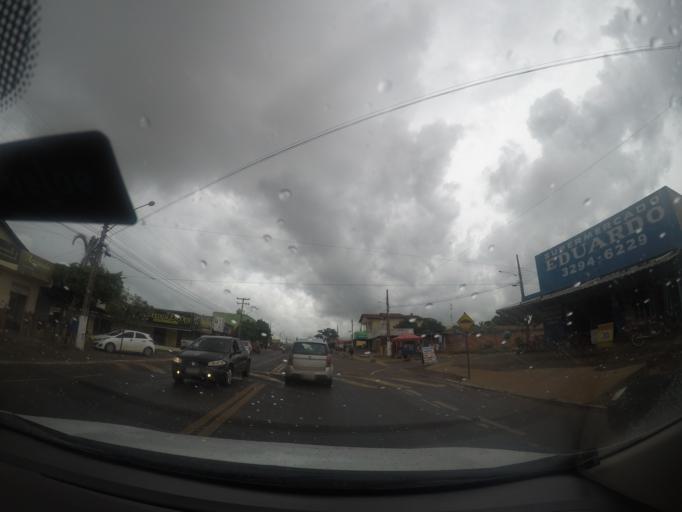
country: BR
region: Goias
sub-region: Trindade
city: Trindade
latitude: -16.6383
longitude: -49.3903
